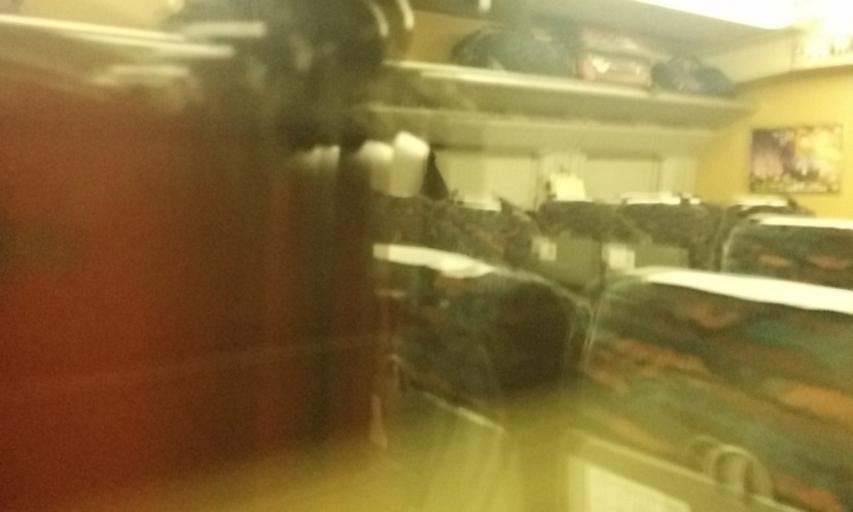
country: JP
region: Fukushima
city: Sukagawa
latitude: 37.2783
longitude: 140.3232
